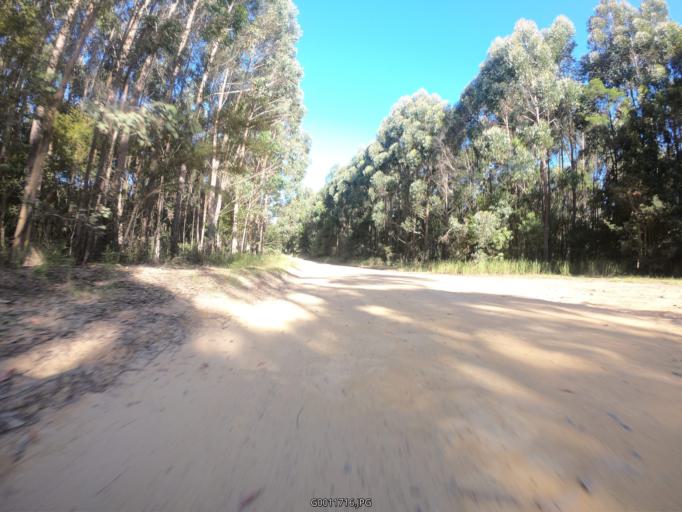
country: AU
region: New South Wales
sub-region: Lake Macquarie Shire
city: Cooranbong
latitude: -33.0601
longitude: 151.3263
